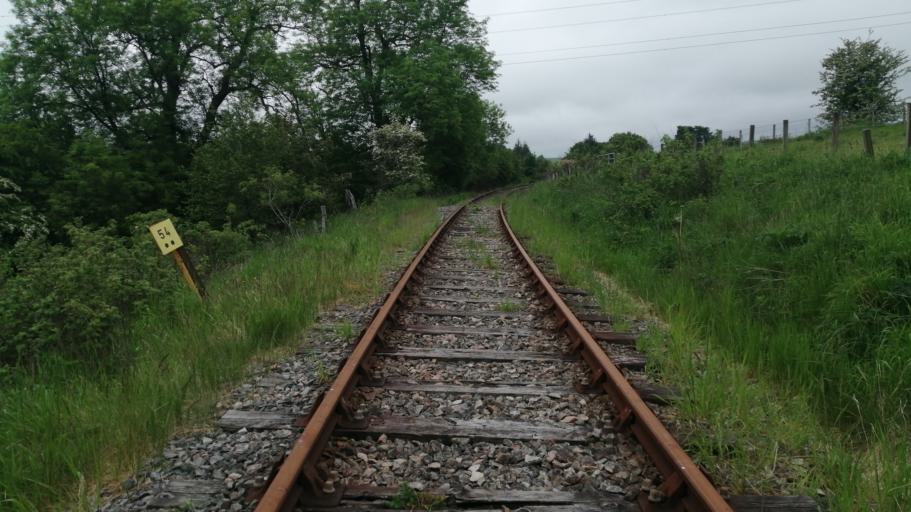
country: GB
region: Scotland
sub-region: Moray
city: Keith
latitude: 57.5351
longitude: -2.9625
